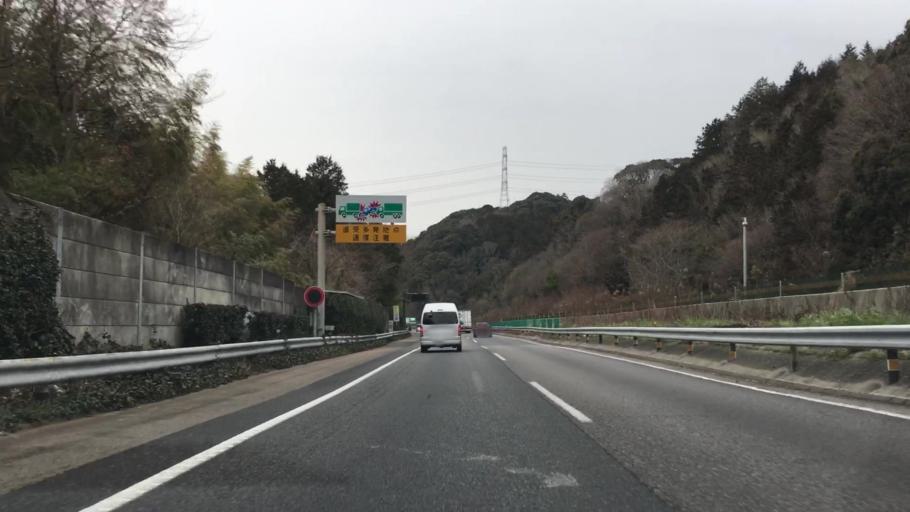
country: JP
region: Aichi
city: Gamagori
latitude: 34.9074
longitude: 137.2484
